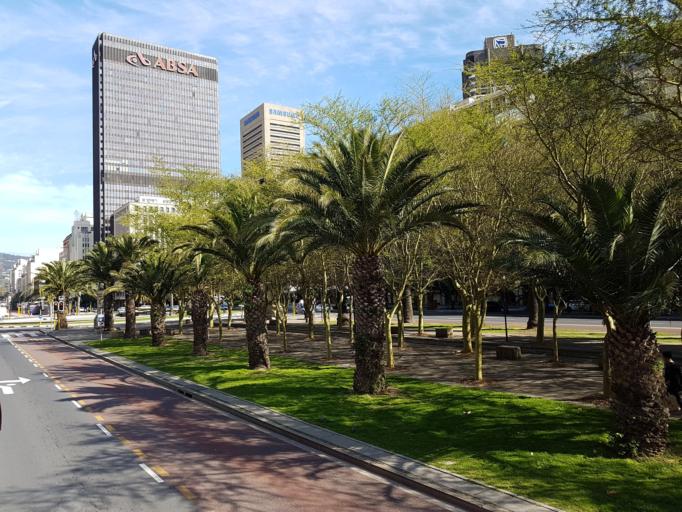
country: ZA
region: Western Cape
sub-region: City of Cape Town
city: Cape Town
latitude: -33.9191
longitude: 18.4266
